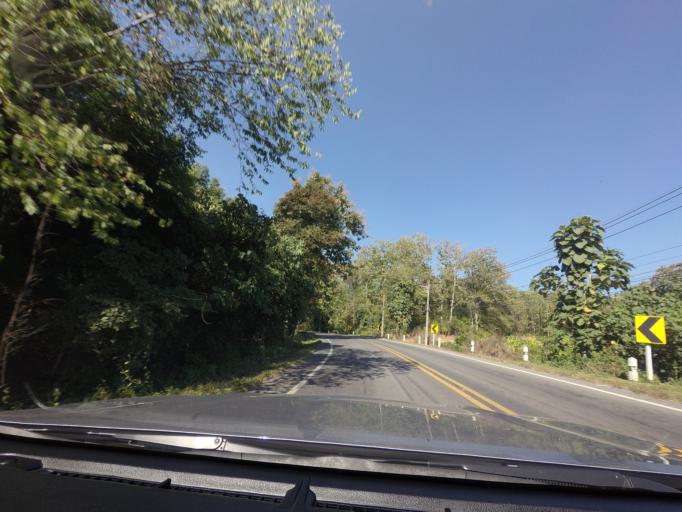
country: TH
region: Sukhothai
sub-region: Amphoe Si Satchanalai
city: Si Satchanalai
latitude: 17.6148
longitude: 99.7091
